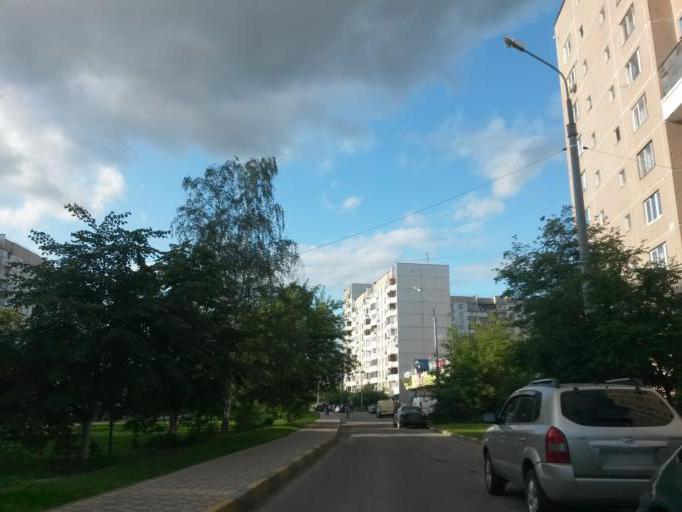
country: RU
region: Moscow
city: Zhulebino
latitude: 55.6902
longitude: 37.8541
